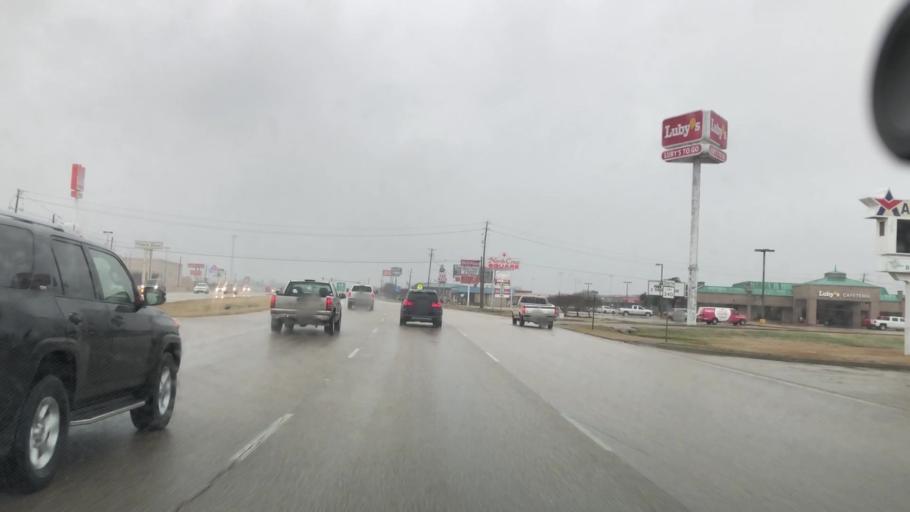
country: US
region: Texas
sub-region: McLennan County
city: Bellmead
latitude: 31.6039
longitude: -97.1054
